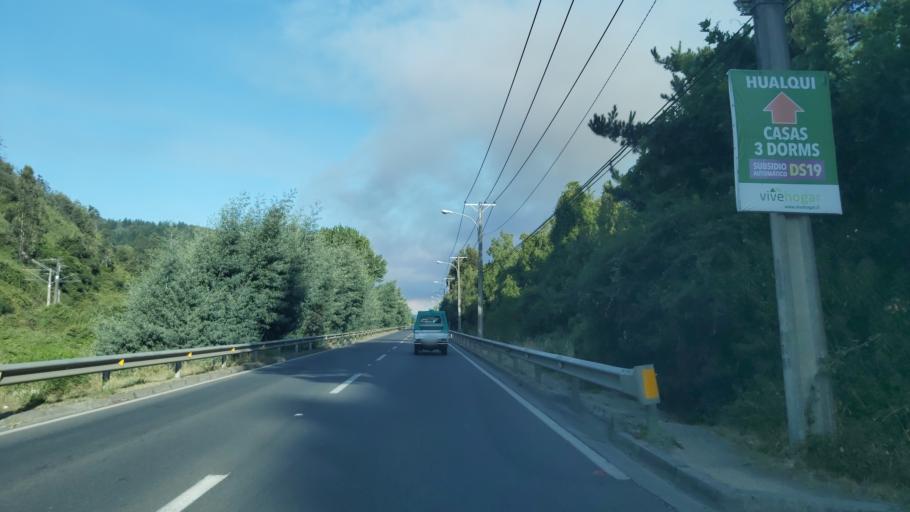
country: CL
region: Biobio
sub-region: Provincia de Concepcion
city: Chiguayante
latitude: -36.9657
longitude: -73.0030
